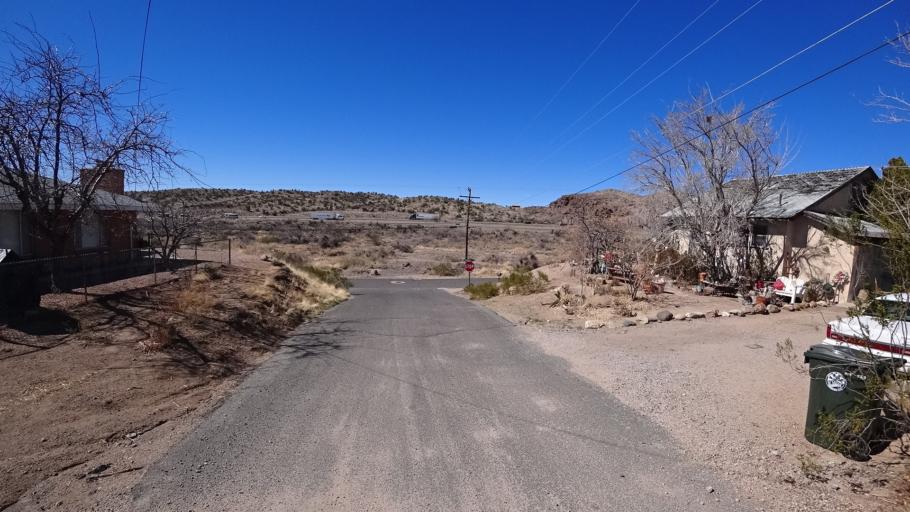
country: US
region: Arizona
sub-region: Mohave County
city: Kingman
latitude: 35.1993
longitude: -114.0640
